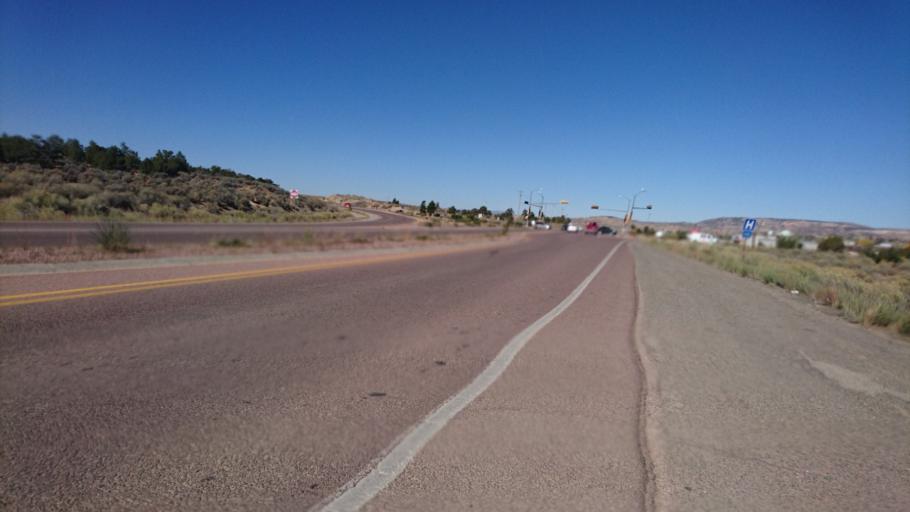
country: US
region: New Mexico
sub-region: McKinley County
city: Gallup
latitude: 35.5012
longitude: -108.7395
